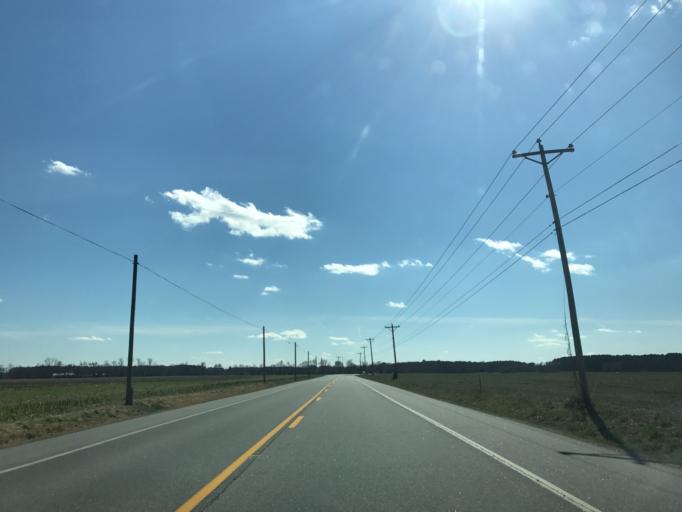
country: US
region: Maryland
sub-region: Kent County
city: Rock Hall
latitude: 39.1679
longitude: -76.2001
